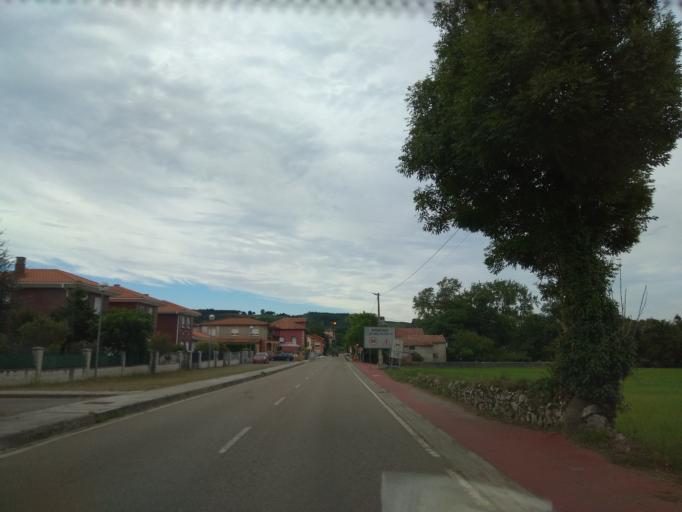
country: ES
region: Cantabria
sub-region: Provincia de Cantabria
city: Hazas de Cesto
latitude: 43.3928
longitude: -3.5889
